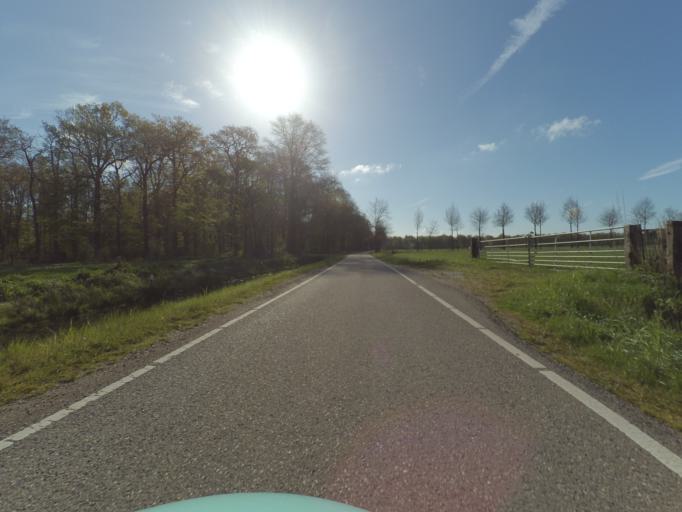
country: NL
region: Utrecht
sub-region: Gemeente Utrechtse Heuvelrug
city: Doorn
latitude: 52.0257
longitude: 5.3177
